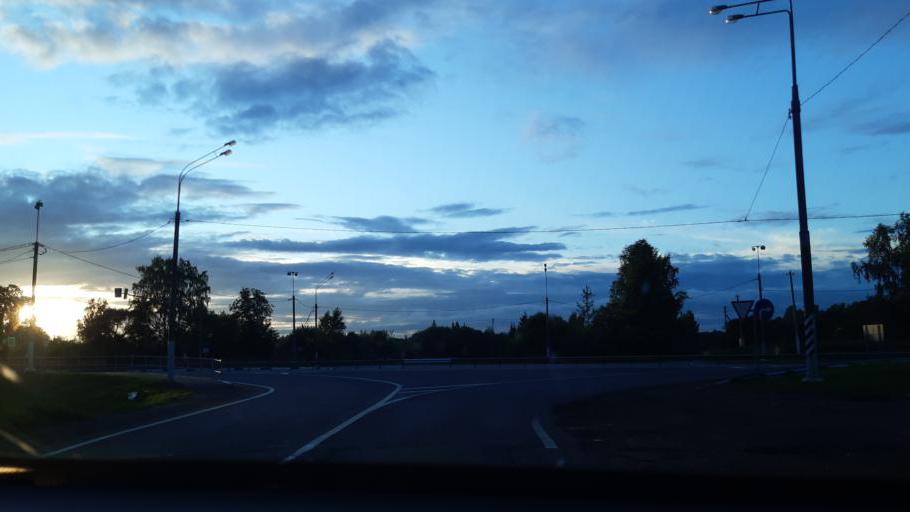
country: RU
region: Smolensk
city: Safonovo
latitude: 55.1320
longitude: 33.1976
